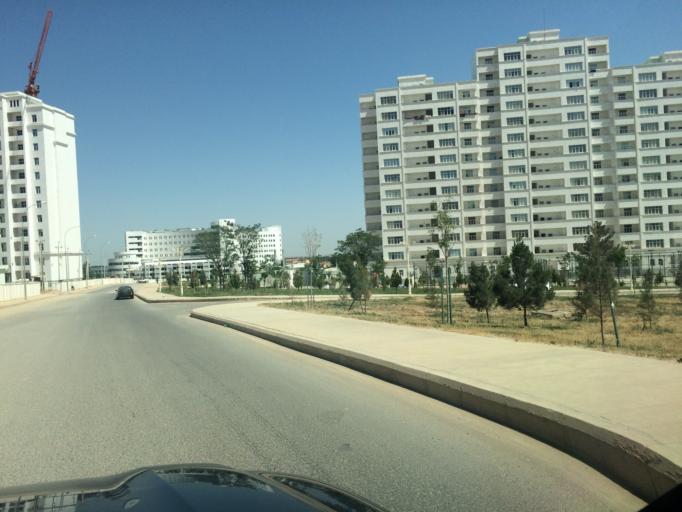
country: TM
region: Ahal
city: Ashgabat
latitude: 37.9373
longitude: 58.3627
